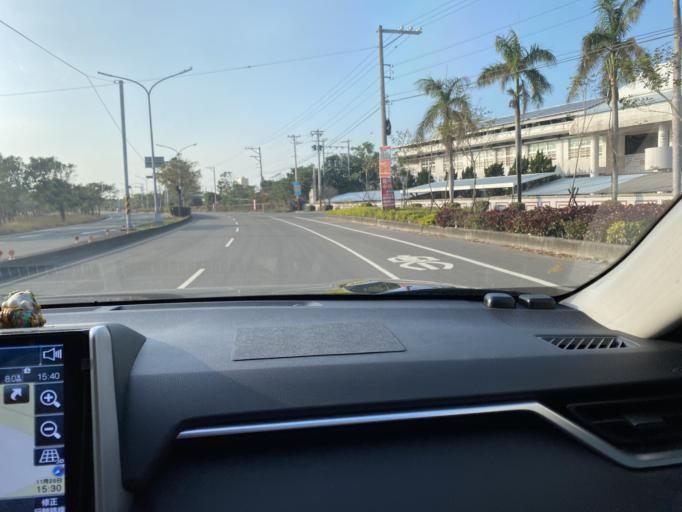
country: TW
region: Taiwan
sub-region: Changhua
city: Chang-hua
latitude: 23.9555
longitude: 120.4153
